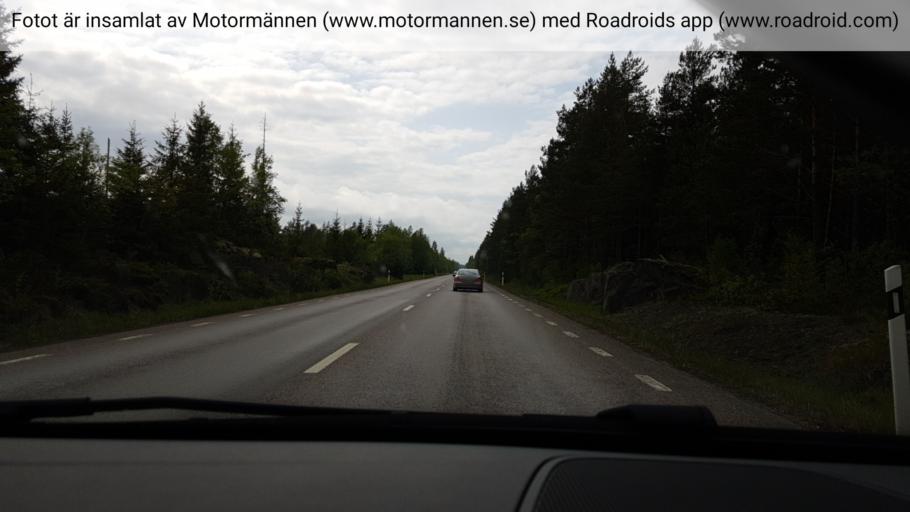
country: SE
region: Uppsala
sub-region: Osthammars Kommun
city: Gimo
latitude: 60.1633
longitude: 18.0691
